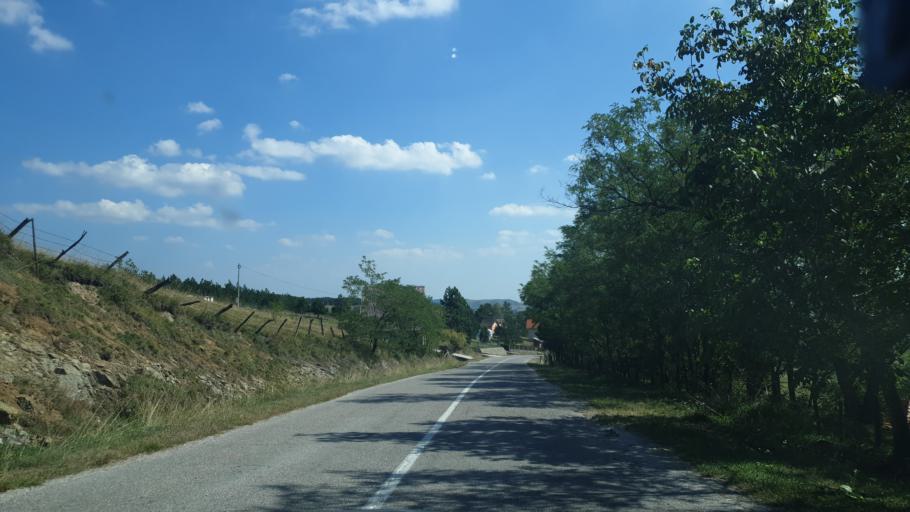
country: RS
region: Central Serbia
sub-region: Zlatiborski Okrug
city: Kosjeric
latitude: 44.0788
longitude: 20.0198
